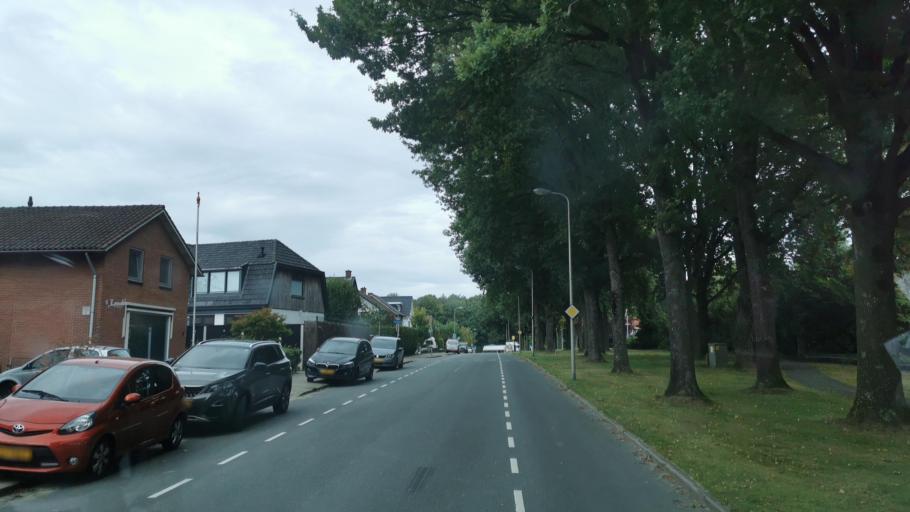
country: NL
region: Overijssel
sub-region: Gemeente Oldenzaal
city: Oldenzaal
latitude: 52.3158
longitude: 6.9412
